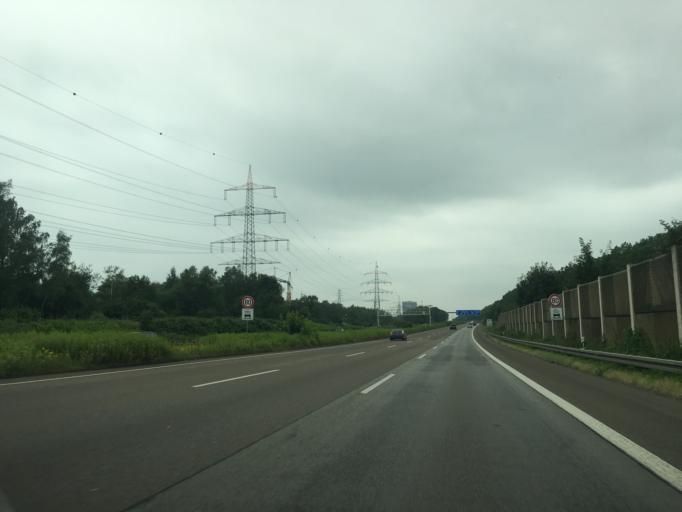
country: DE
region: North Rhine-Westphalia
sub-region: Regierungsbezirk Munster
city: Bottrop
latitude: 51.4981
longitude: 6.9115
